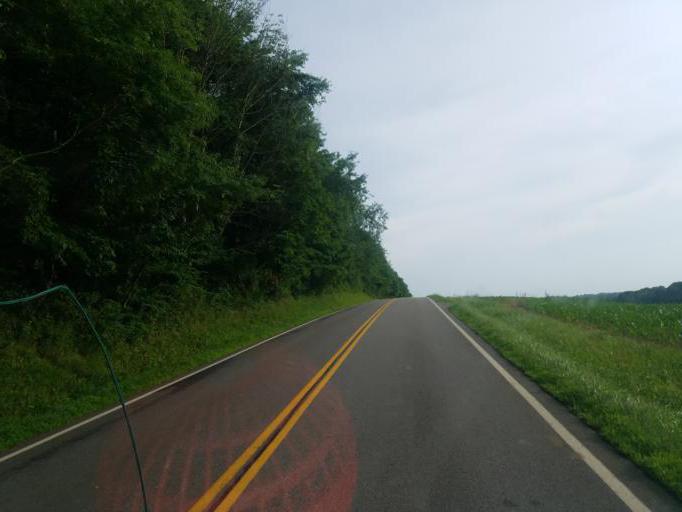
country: US
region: Ohio
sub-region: Ashland County
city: Loudonville
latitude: 40.7438
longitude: -82.2832
